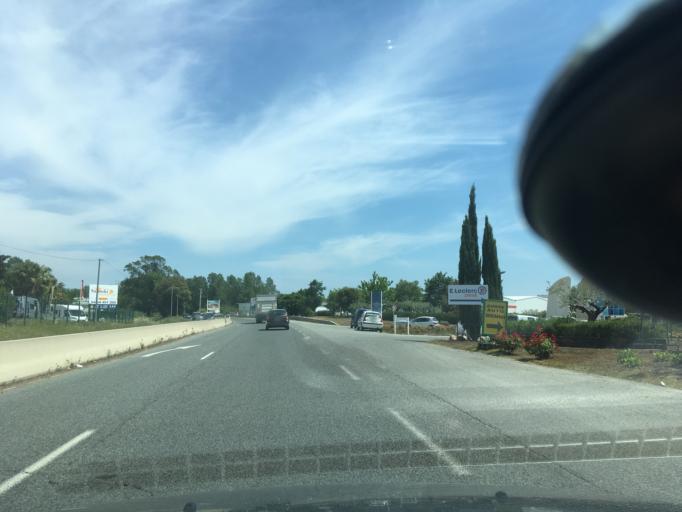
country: FR
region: Provence-Alpes-Cote d'Azur
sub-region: Departement du Var
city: Roquebrune-sur-Argens
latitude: 43.4628
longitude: 6.6436
